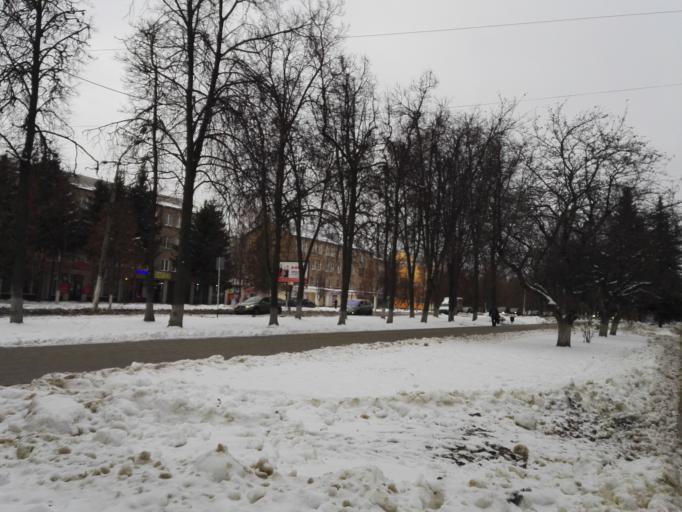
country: RU
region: Tula
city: Novomoskovsk
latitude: 54.0113
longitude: 38.2964
